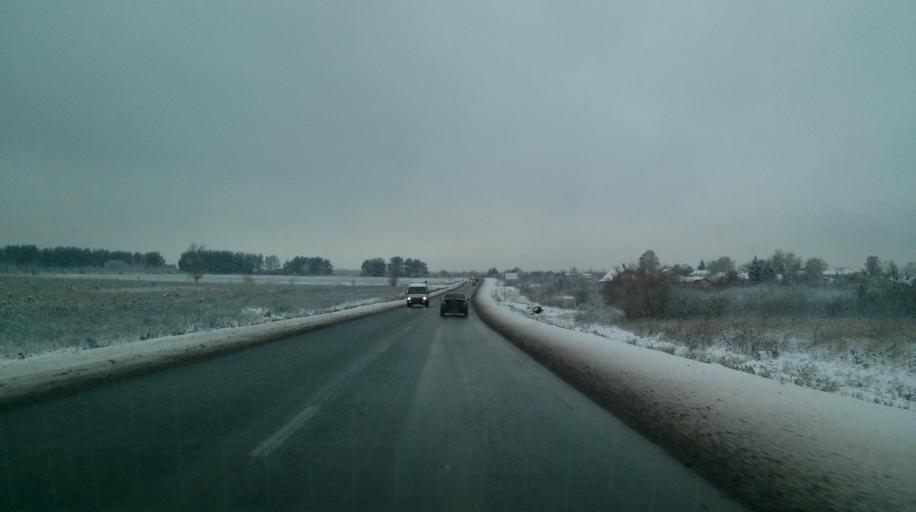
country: RU
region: Nizjnij Novgorod
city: Bogorodsk
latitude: 56.0872
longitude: 43.5235
